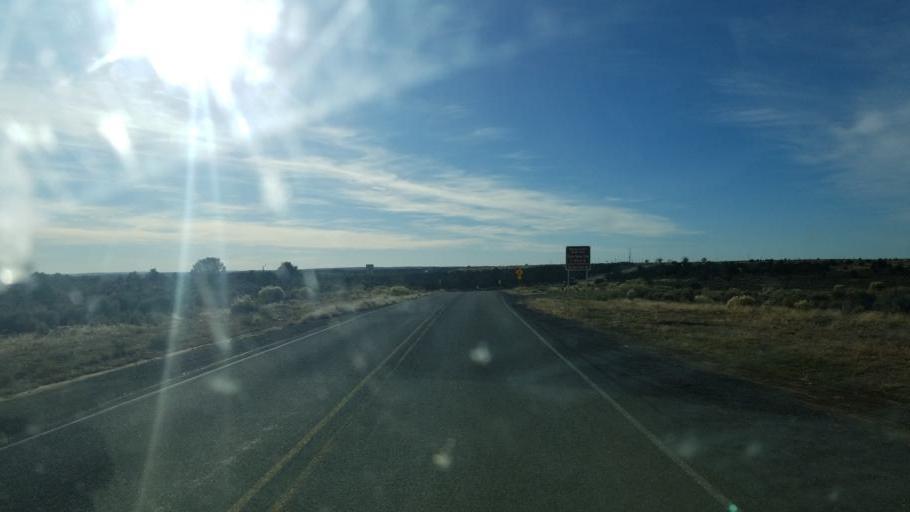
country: US
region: New Mexico
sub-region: Rio Arriba County
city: Navajo
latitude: 36.7025
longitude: -107.3772
